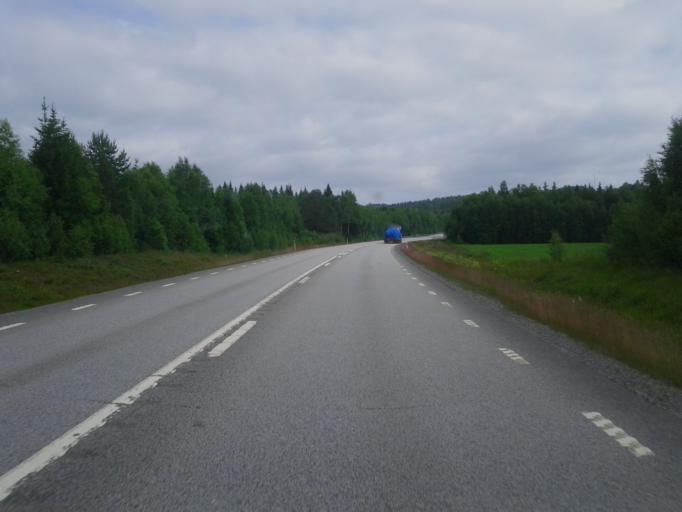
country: SE
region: Vaesterbotten
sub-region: Robertsfors Kommun
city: Robertsfors
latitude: 64.2913
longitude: 21.0785
